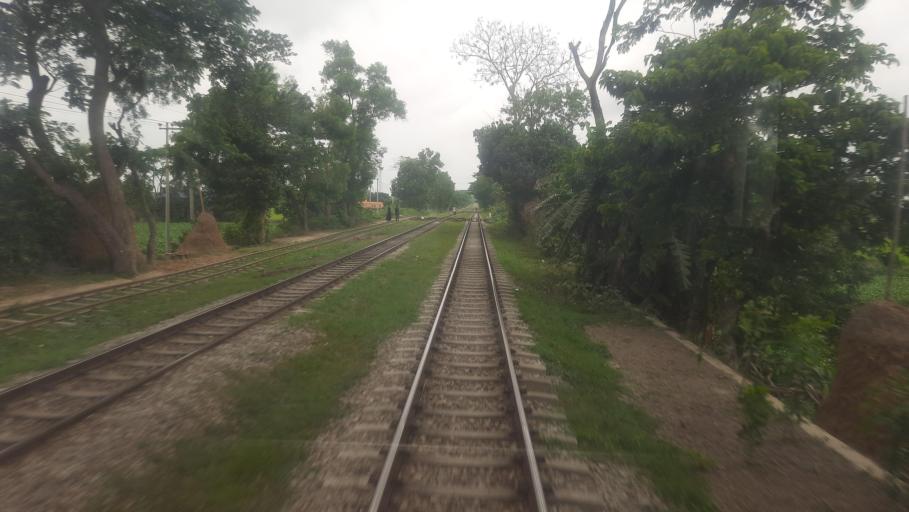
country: BD
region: Dhaka
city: Bhairab Bazar
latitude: 24.0250
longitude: 91.0190
